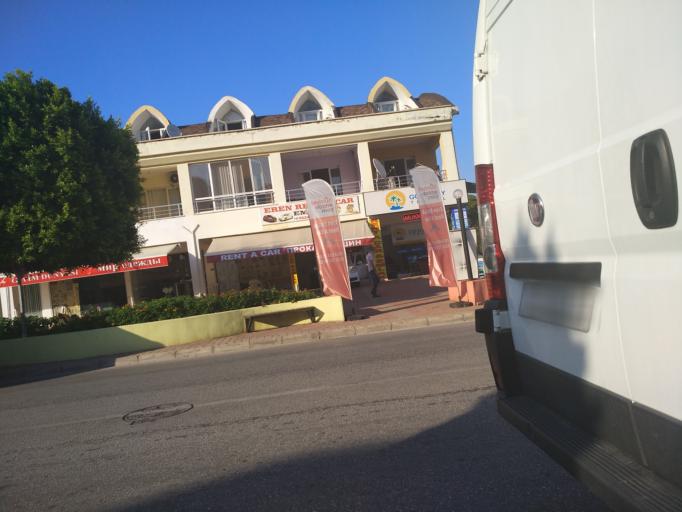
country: TR
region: Antalya
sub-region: Kemer
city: Goeynuek
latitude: 36.6660
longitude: 30.5531
